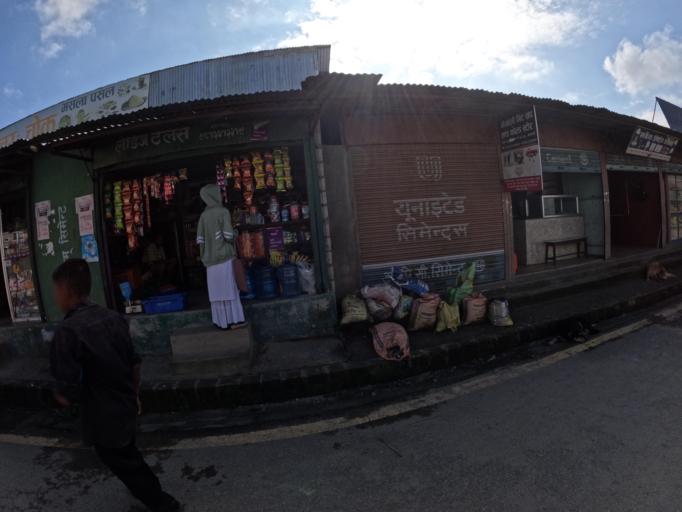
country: NP
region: Central Region
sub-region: Bagmati Zone
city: Kathmandu
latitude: 27.7608
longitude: 85.3332
